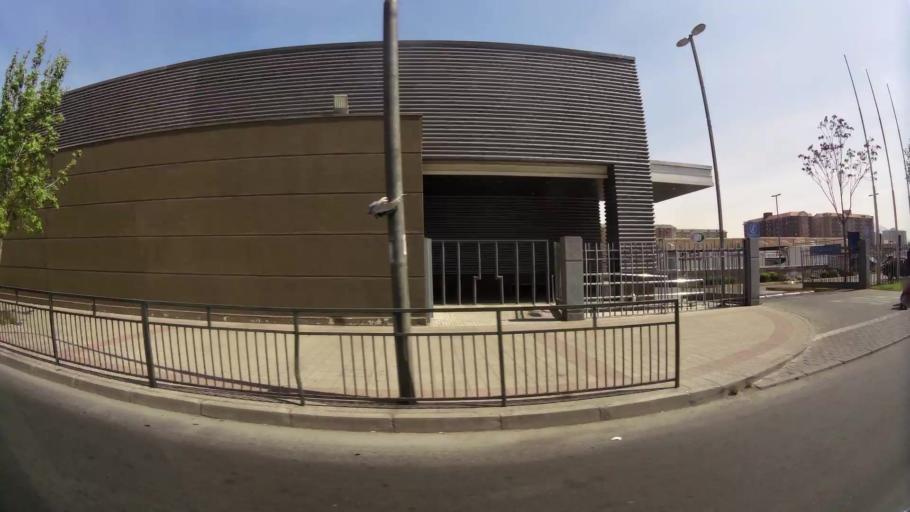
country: CL
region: Santiago Metropolitan
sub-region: Provincia de Santiago
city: Santiago
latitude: -33.4319
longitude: -70.6807
